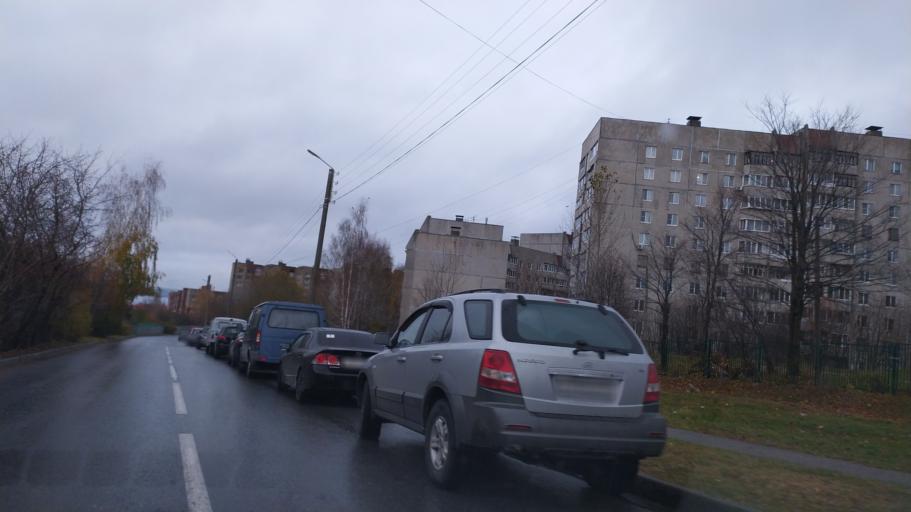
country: RU
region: Chuvashia
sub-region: Cheboksarskiy Rayon
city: Cheboksary
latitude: 56.1464
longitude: 47.1619
